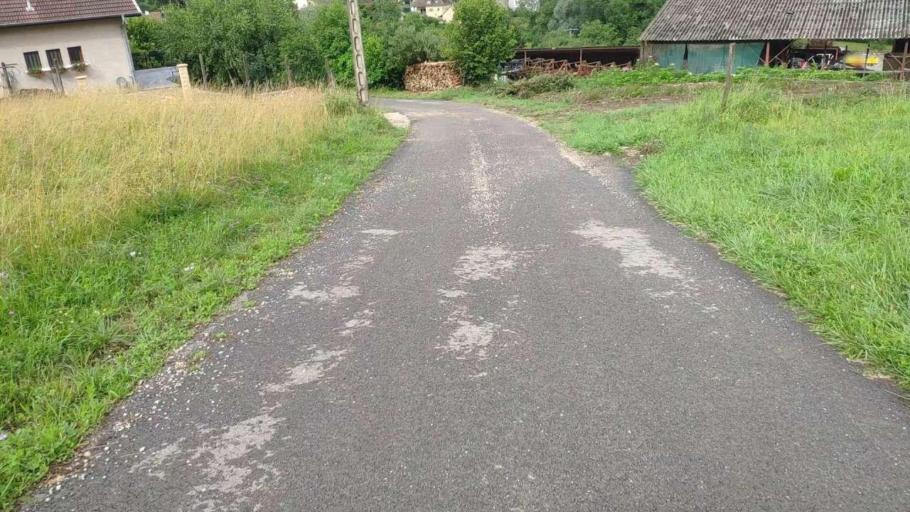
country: FR
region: Franche-Comte
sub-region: Departement du Jura
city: Poligny
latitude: 46.8042
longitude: 5.5922
